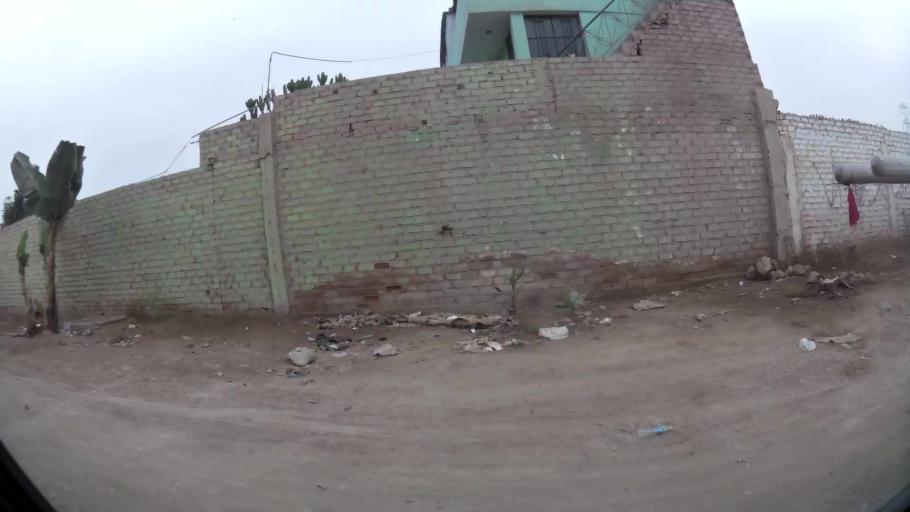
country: PE
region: Lima
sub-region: Lima
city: Independencia
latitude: -11.9694
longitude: -77.0900
